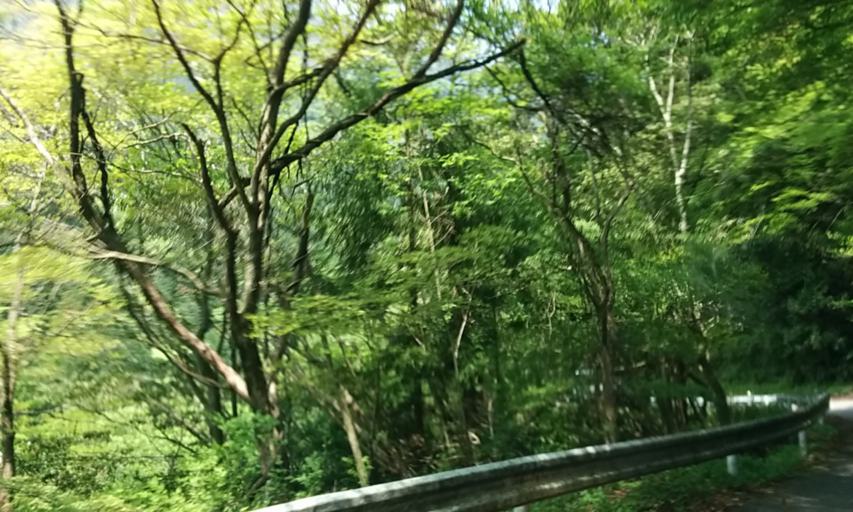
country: JP
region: Ehime
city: Niihama
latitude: 33.8685
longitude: 133.2942
